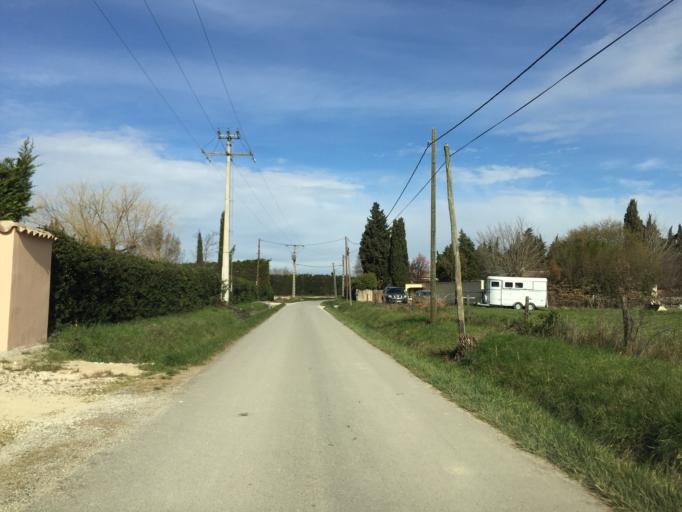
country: FR
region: Provence-Alpes-Cote d'Azur
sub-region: Departement du Vaucluse
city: Caderousse
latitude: 44.1179
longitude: 4.7424
